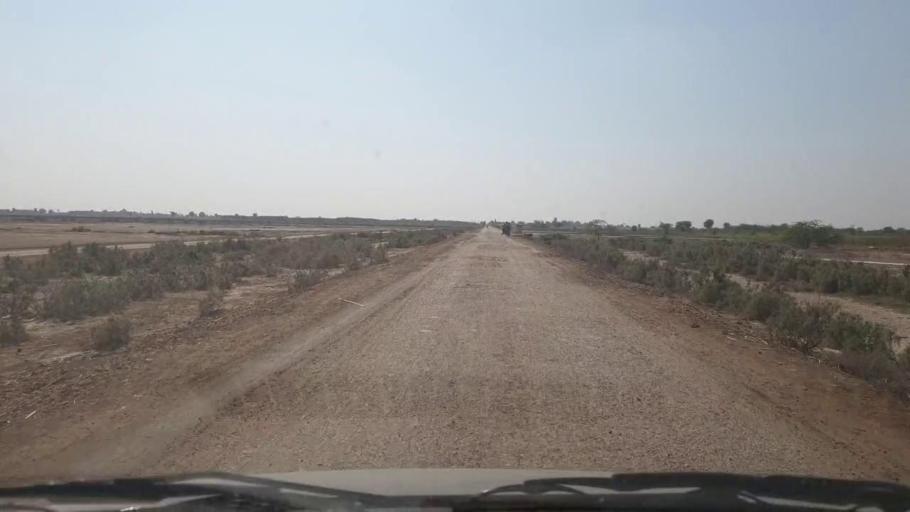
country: PK
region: Sindh
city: Samaro
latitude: 25.2403
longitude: 69.3413
